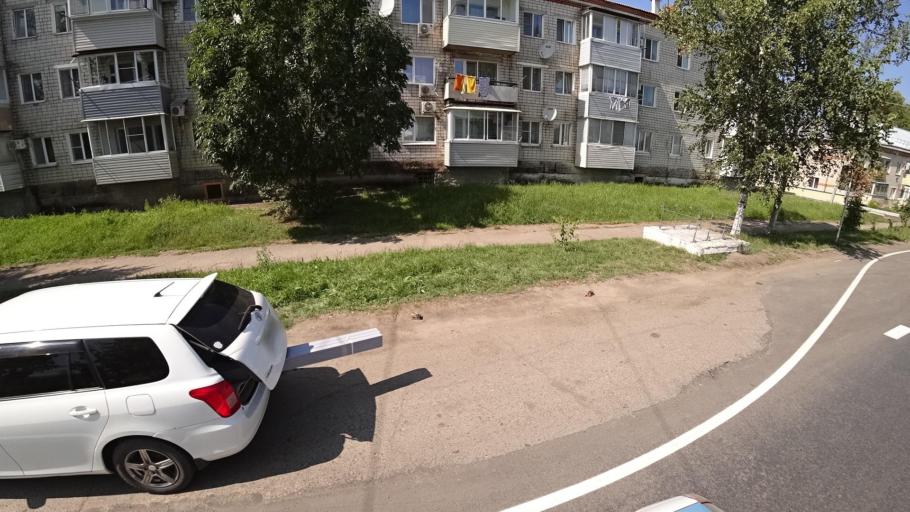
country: RU
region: Khabarovsk Krai
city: Khor
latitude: 47.9701
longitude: 135.0546
